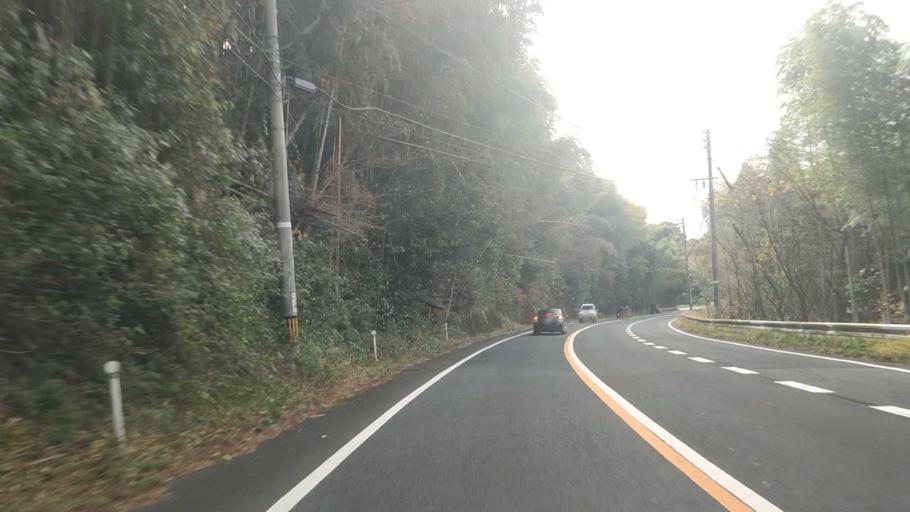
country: JP
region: Kagoshima
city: Kajiki
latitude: 31.7619
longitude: 130.6807
